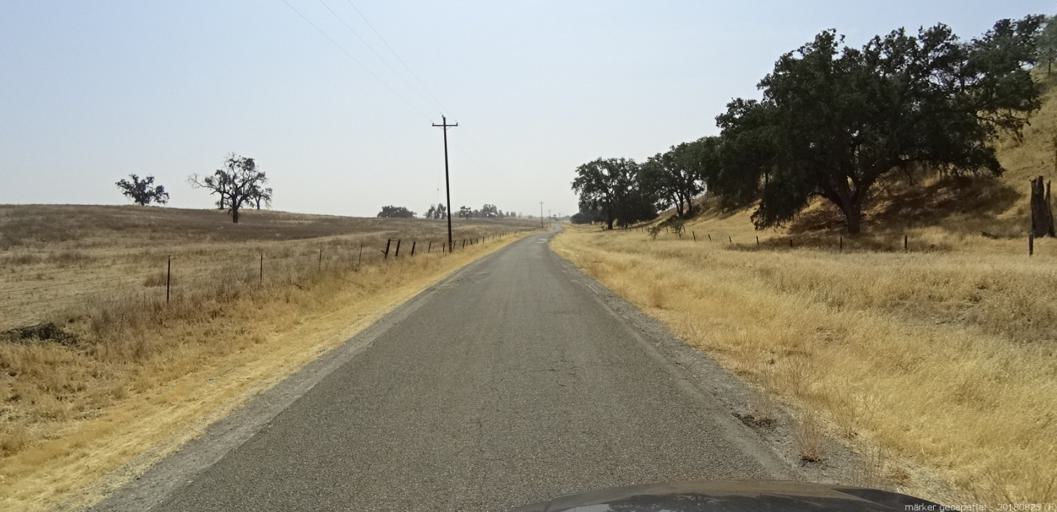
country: US
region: California
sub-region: San Luis Obispo County
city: Shandon
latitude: 35.8580
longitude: -120.3913
